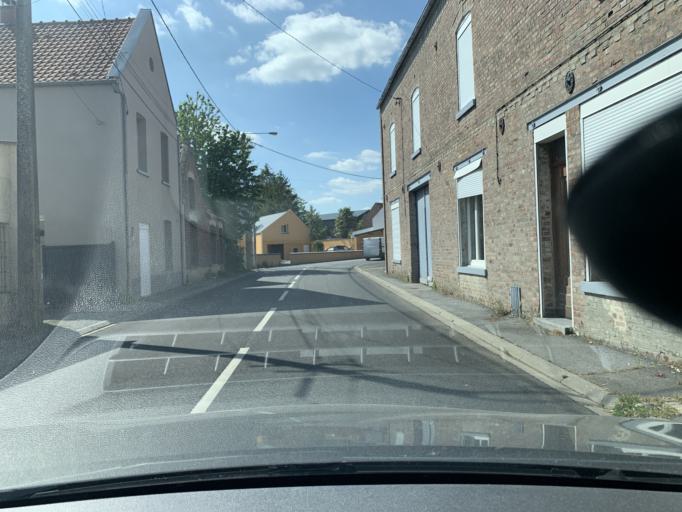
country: FR
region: Nord-Pas-de-Calais
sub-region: Departement du Pas-de-Calais
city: Oisy-le-Verger
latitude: 50.2512
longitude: 3.1179
